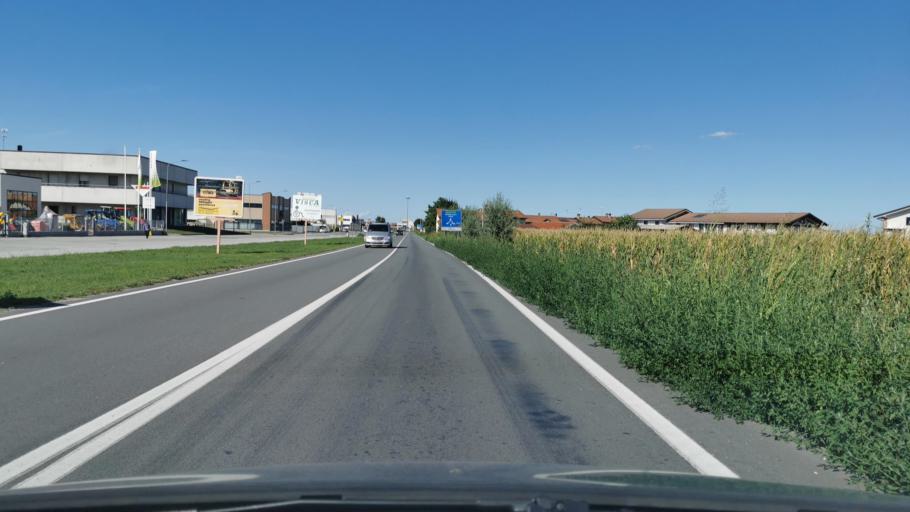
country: IT
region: Piedmont
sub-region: Provincia di Cuneo
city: Genola
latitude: 44.5894
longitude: 7.6557
